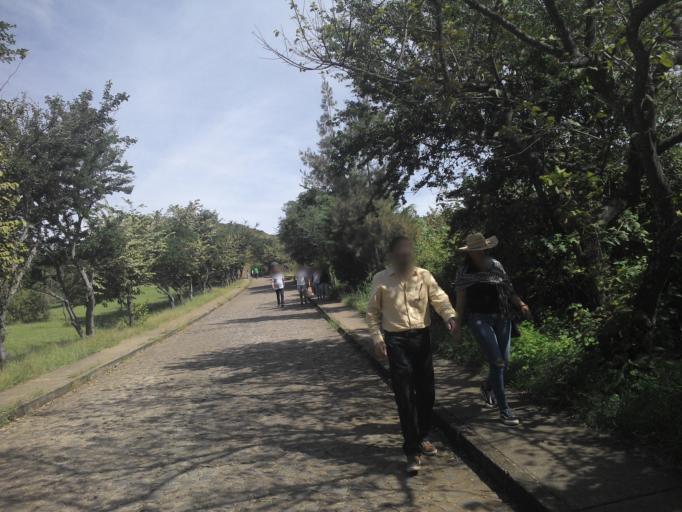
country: MX
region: Jalisco
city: Teuchitlan
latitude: 20.6954
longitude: -103.8375
